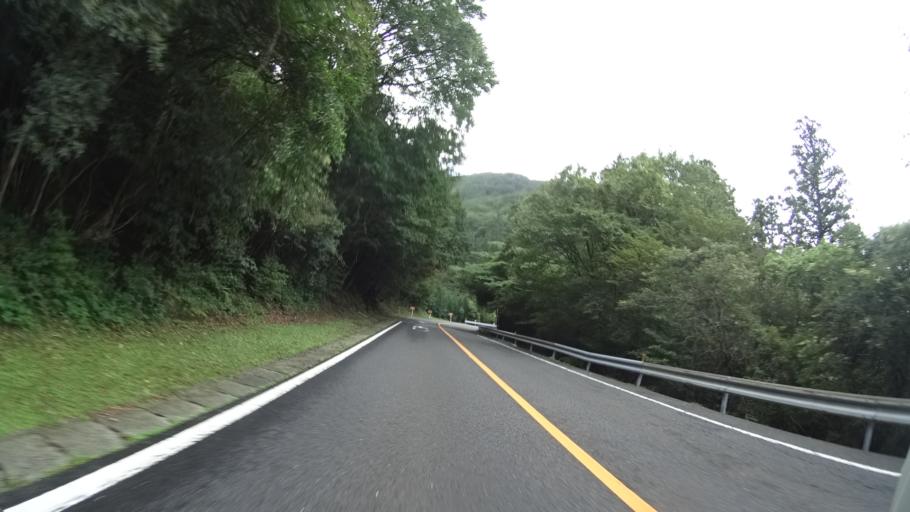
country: JP
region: Oita
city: Tsukawaki
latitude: 33.0987
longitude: 131.2217
